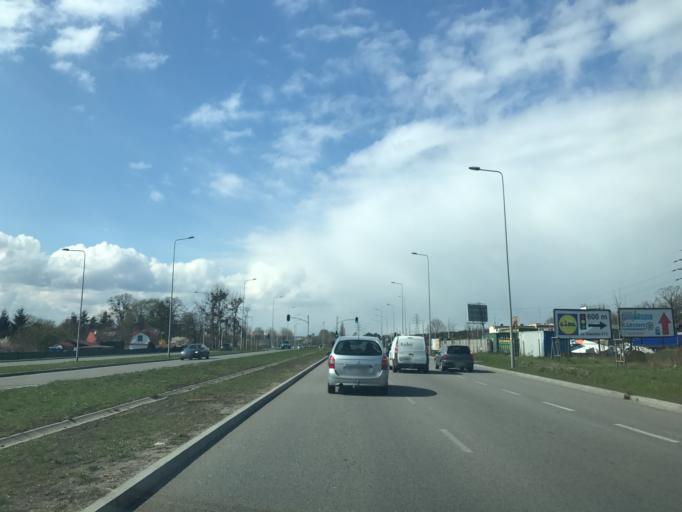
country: PL
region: Pomeranian Voivodeship
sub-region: Gdansk
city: Gdansk
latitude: 54.3989
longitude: 18.6282
